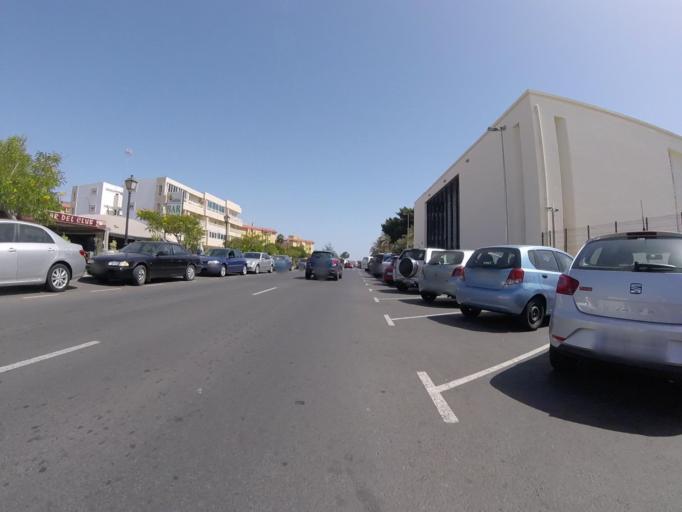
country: ES
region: Canary Islands
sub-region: Provincia de Las Palmas
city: Maspalomas
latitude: 27.7662
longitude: -15.5808
